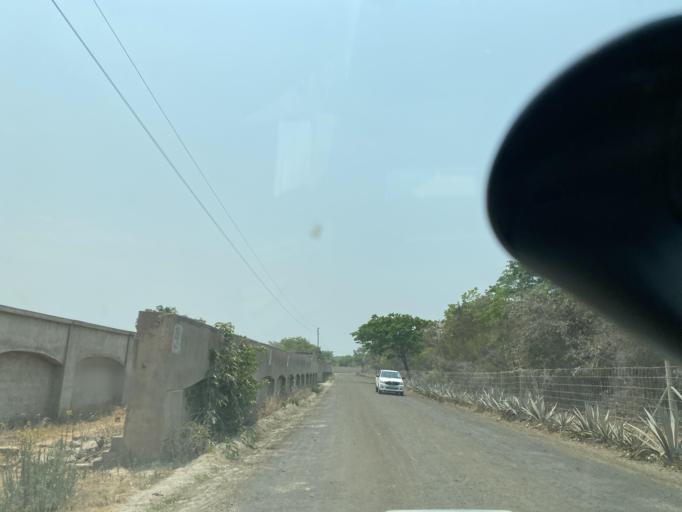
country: ZM
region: Lusaka
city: Lusaka
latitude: -15.5119
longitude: 28.4440
